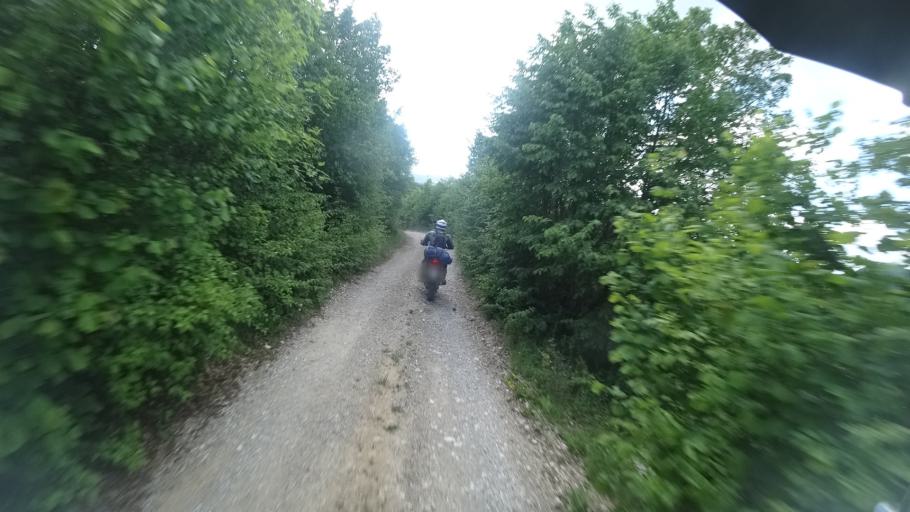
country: HR
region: Zadarska
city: Gracac
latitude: 44.2789
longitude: 15.9355
